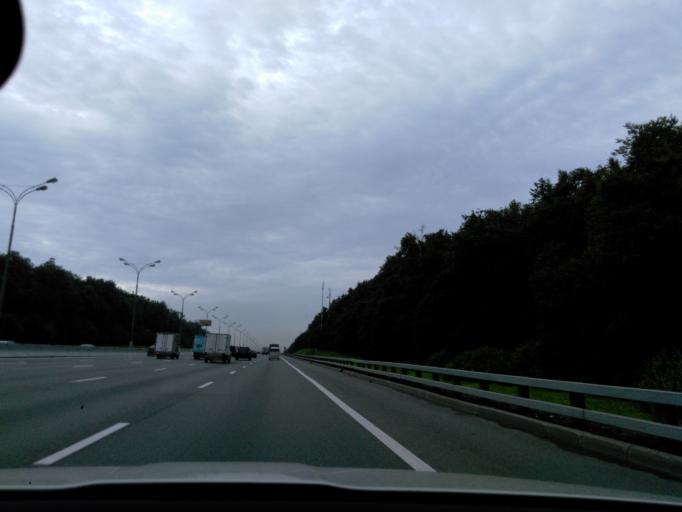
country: RU
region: Moscow
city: Gol'yanovo
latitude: 55.8405
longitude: 37.8070
